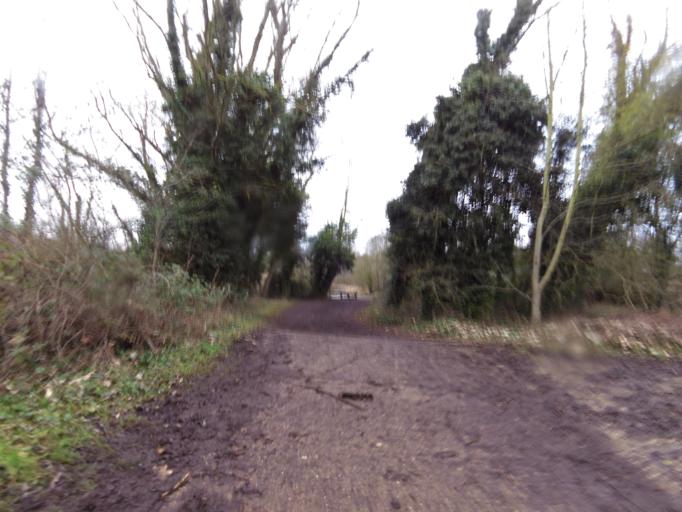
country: GB
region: England
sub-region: Cambridgeshire
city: Waterbeach
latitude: 52.2375
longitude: 0.1681
